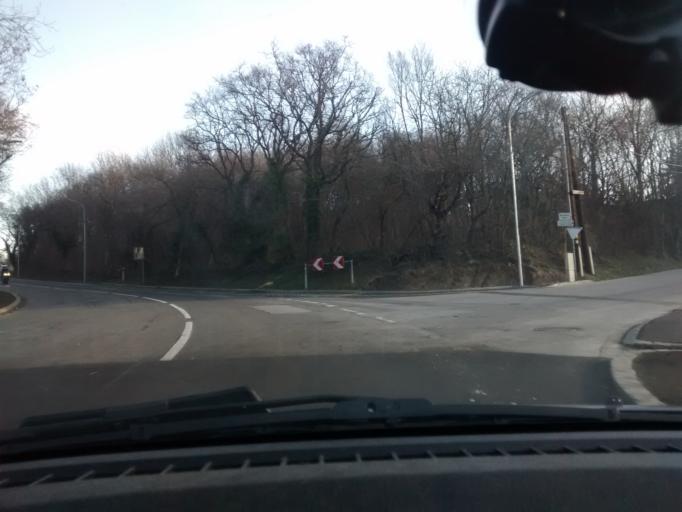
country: AT
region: Lower Austria
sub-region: Politischer Bezirk Modling
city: Hinterbruehl
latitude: 48.0896
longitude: 16.2619
